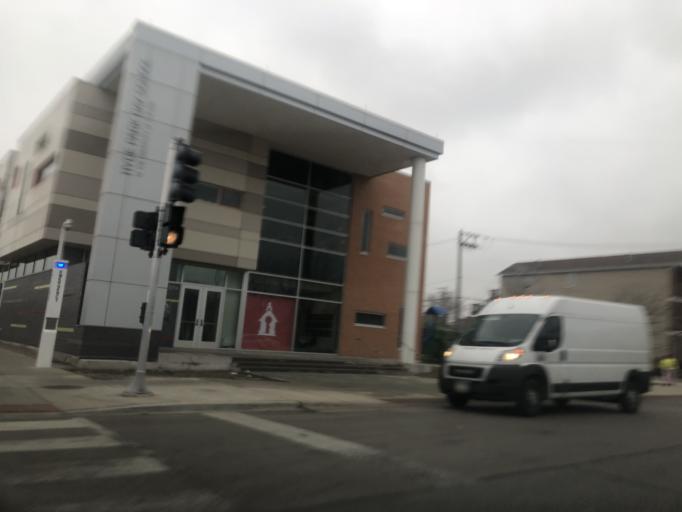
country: US
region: Illinois
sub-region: Cook County
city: Chicago
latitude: 41.7806
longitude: -87.6010
